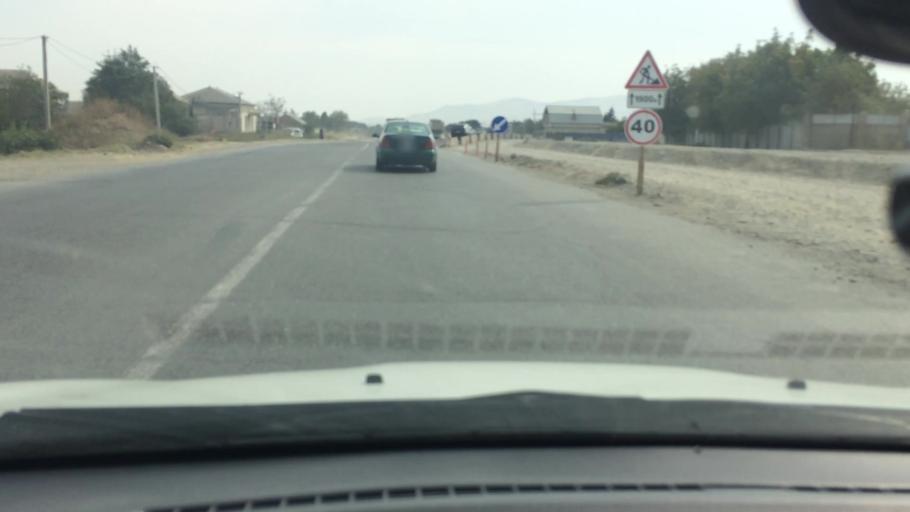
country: GE
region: T'bilisi
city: Tbilisi
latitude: 41.6388
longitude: 44.9156
